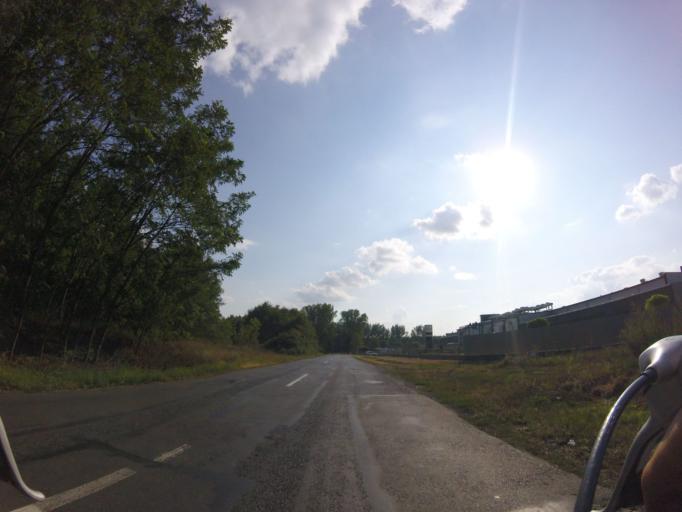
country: HU
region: Szabolcs-Szatmar-Bereg
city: Nyirkarasz
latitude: 48.0823
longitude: 22.0909
